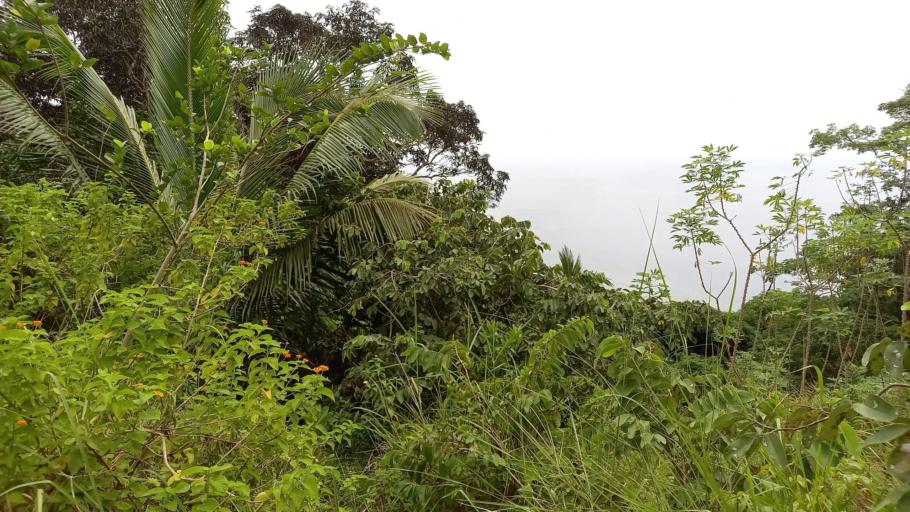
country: YT
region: Acoua
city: Acoua
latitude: -12.7105
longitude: 45.0586
